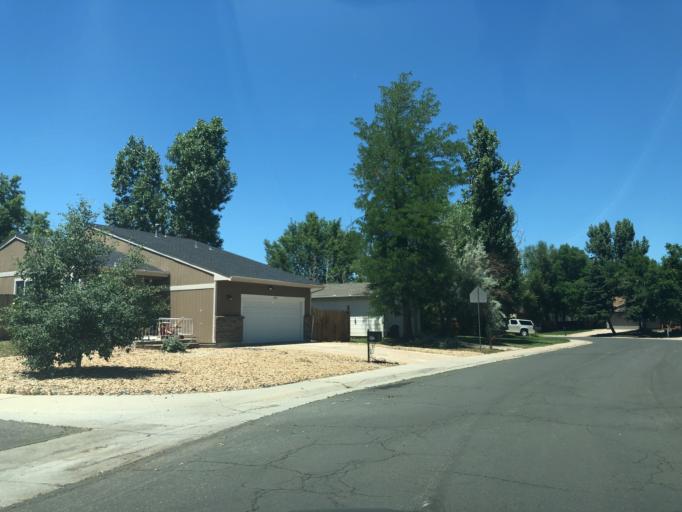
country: US
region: Colorado
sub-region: Arapahoe County
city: Dove Valley
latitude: 39.6198
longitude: -104.7790
